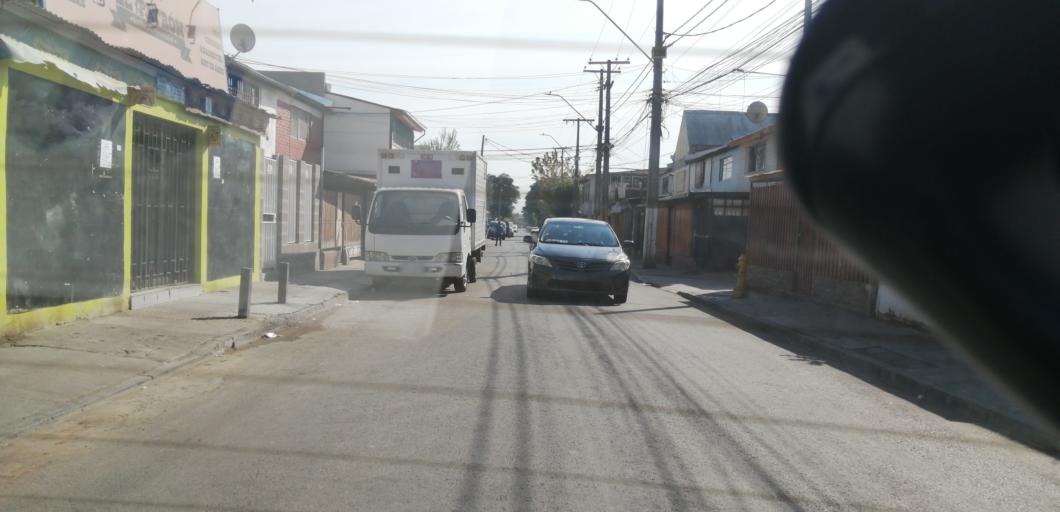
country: CL
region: Santiago Metropolitan
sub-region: Provincia de Santiago
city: Lo Prado
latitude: -33.4640
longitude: -70.7500
